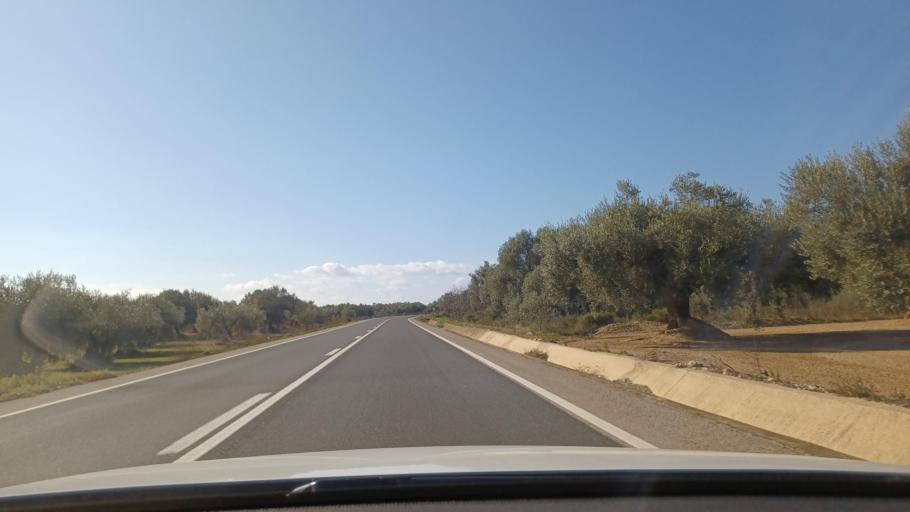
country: ES
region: Catalonia
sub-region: Provincia de Tarragona
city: Ulldecona
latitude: 40.6448
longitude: 0.3812
